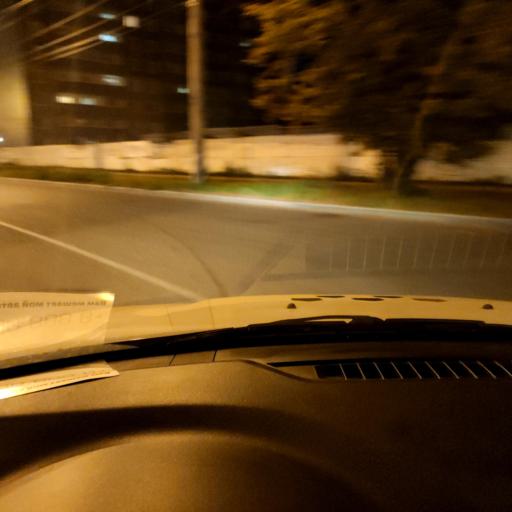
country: RU
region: Samara
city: Tol'yatti
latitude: 53.5225
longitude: 49.4177
